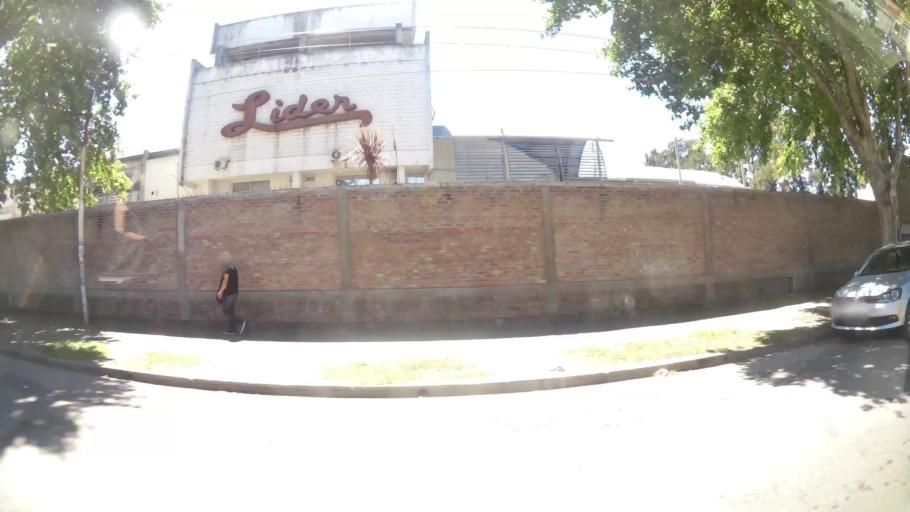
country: AR
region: Santa Fe
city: Perez
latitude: -32.9539
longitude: -60.7119
